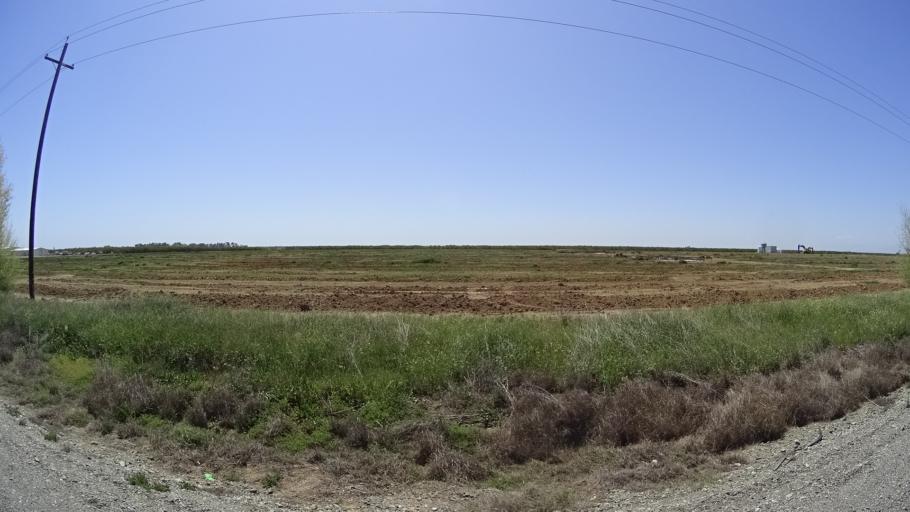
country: US
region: California
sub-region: Glenn County
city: Hamilton City
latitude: 39.7665
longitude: -122.0577
